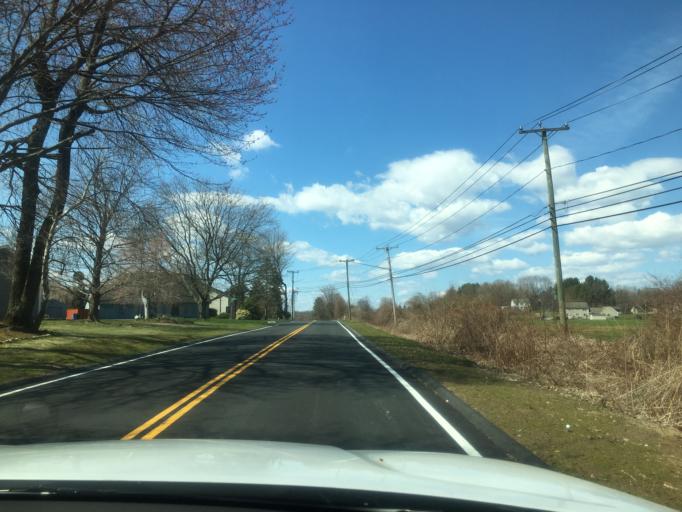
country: US
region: Connecticut
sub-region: Hartford County
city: Hazardville
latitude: 41.9583
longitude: -72.5358
